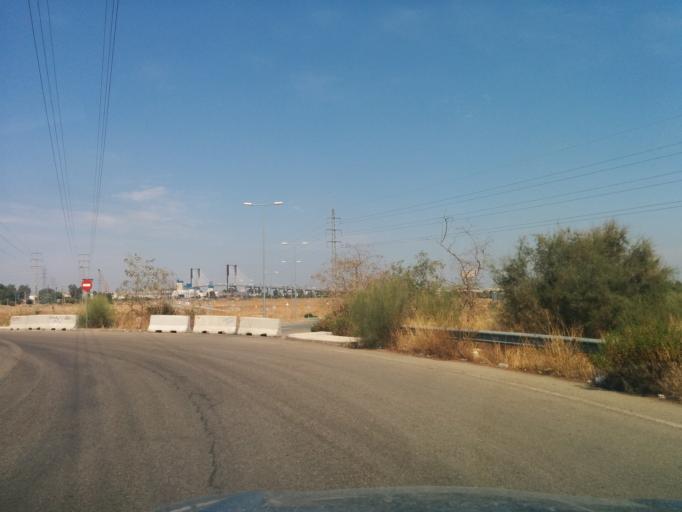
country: ES
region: Andalusia
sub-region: Provincia de Sevilla
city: Gelves
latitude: 37.3320
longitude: -5.9864
